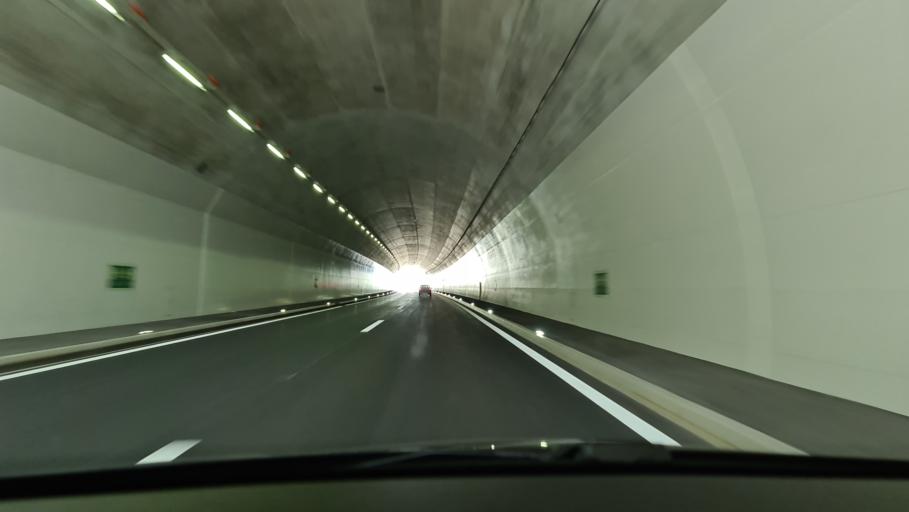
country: CH
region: Bern
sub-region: Jura bernois
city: Bevilard
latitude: 47.2306
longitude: 7.2786
